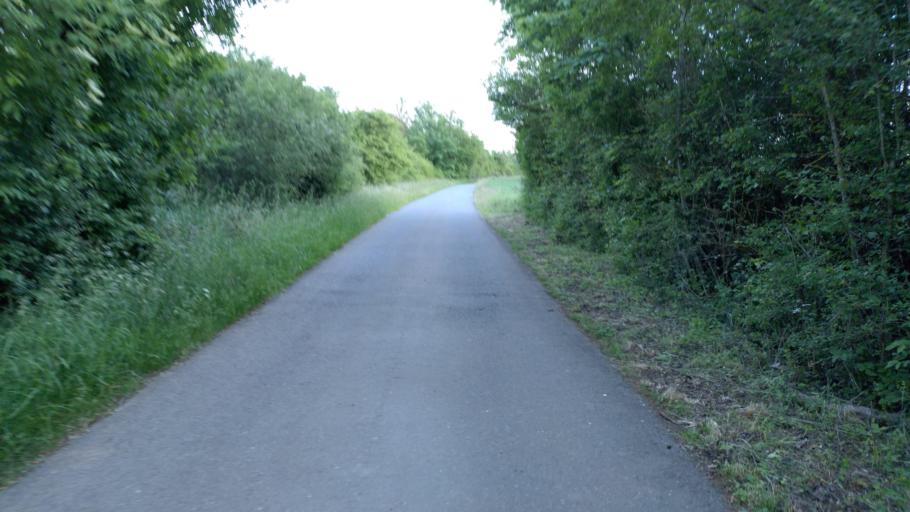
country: DE
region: Bavaria
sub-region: Upper Franconia
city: Bindlach
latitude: 49.9986
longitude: 11.6173
